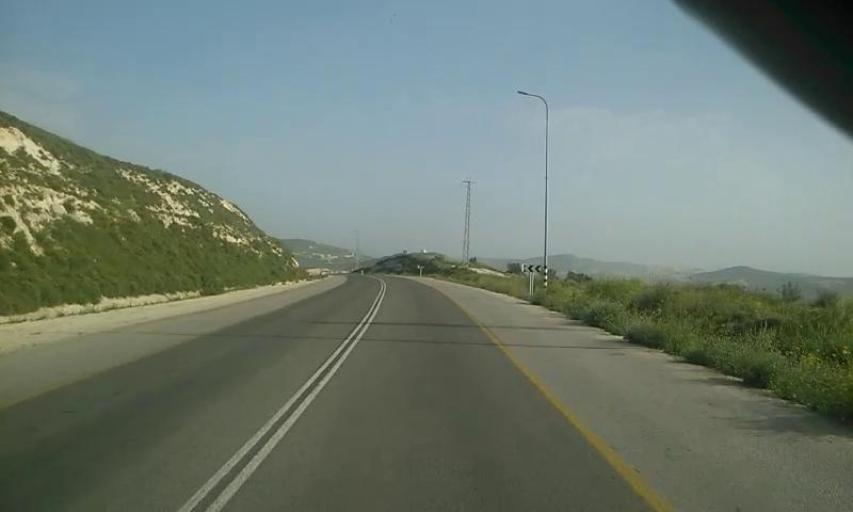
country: PS
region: West Bank
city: Sarrah
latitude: 32.1949
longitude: 35.1873
